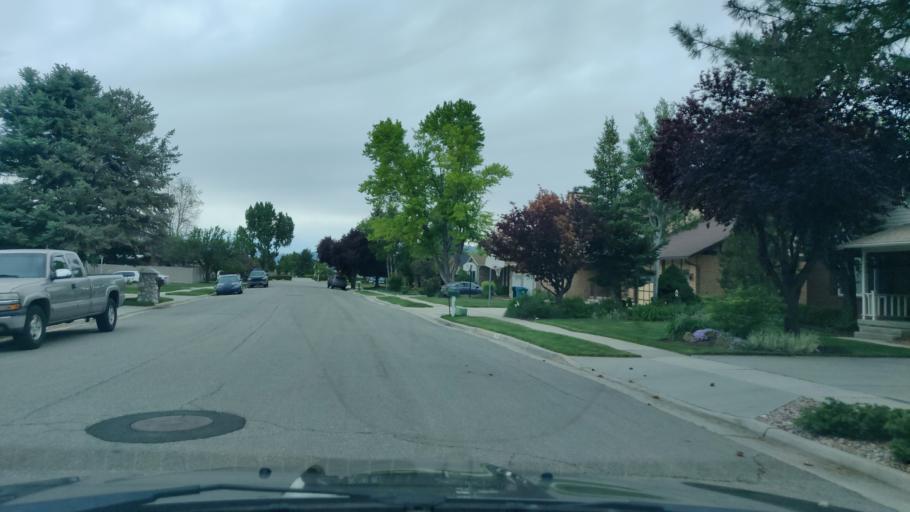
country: US
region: Utah
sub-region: Salt Lake County
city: Little Cottonwood Creek Valley
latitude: 40.6099
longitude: -111.8207
